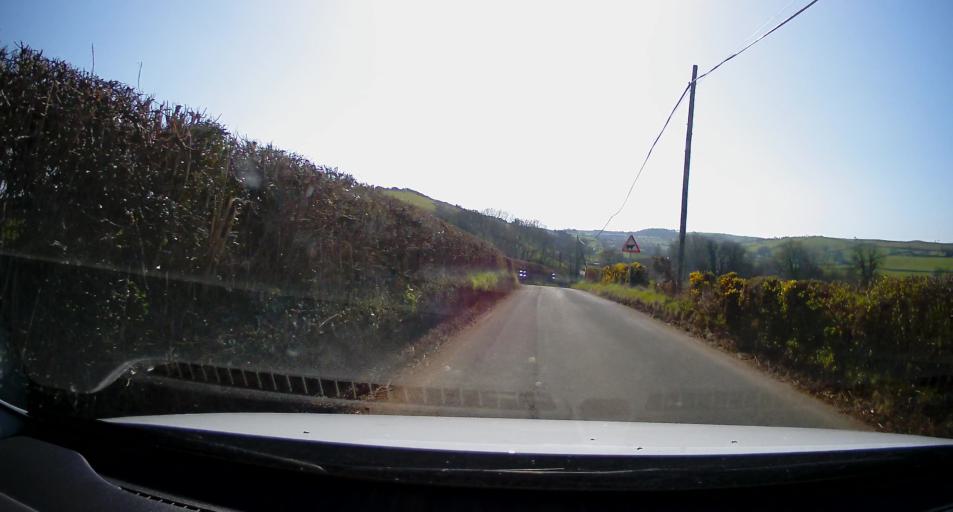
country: GB
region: Wales
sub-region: County of Ceredigion
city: Penparcau
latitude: 52.3497
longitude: -4.0635
